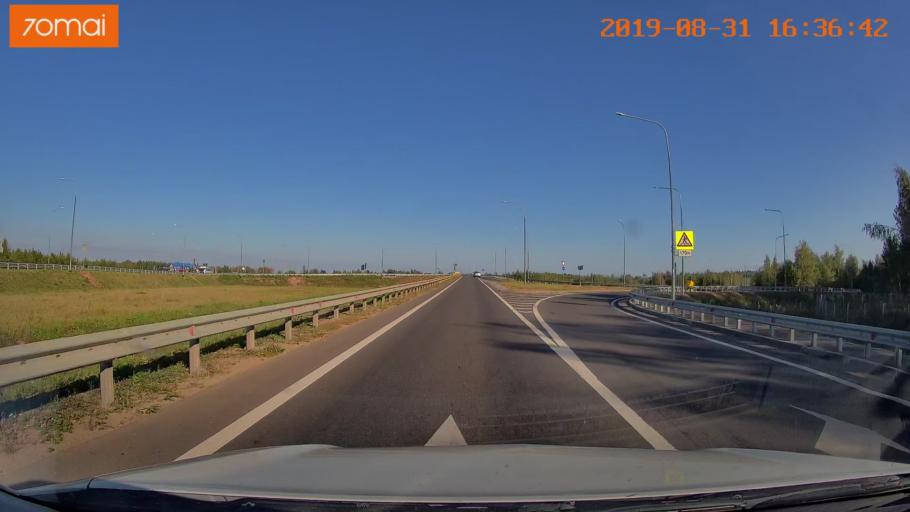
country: RU
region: Kaluga
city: Kurovskoye
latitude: 54.5282
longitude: 35.9804
